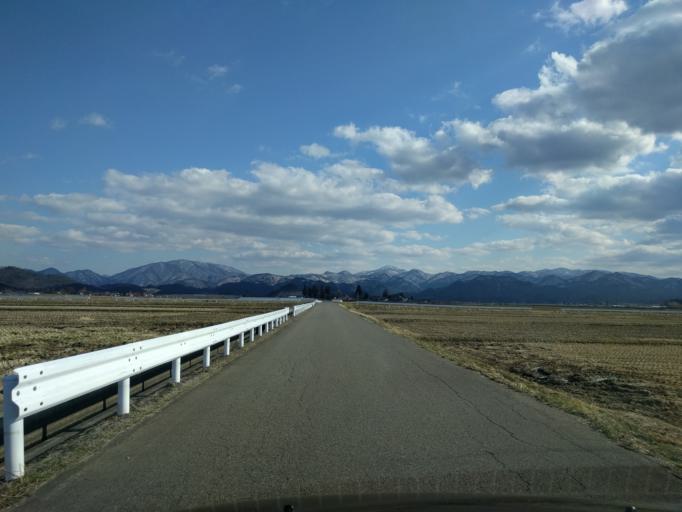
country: JP
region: Fukushima
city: Kitakata
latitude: 37.4694
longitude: 139.8714
